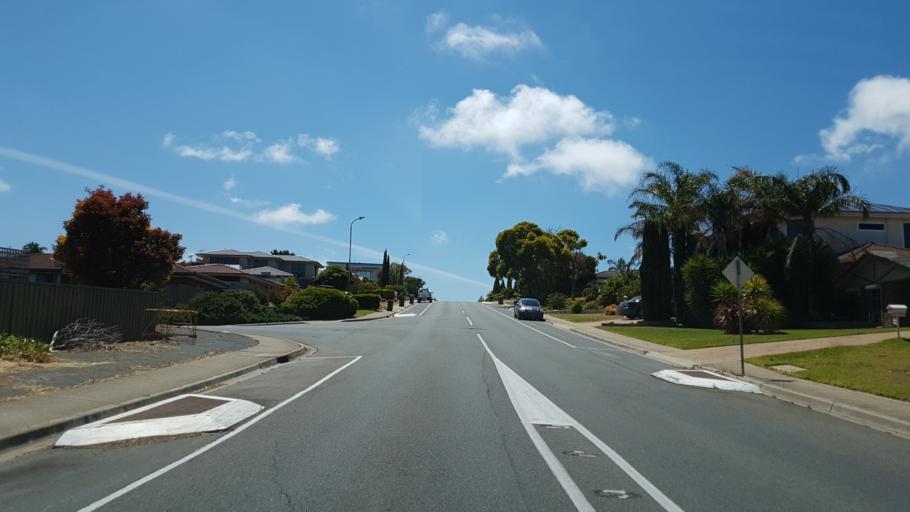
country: AU
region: South Australia
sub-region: Marion
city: Happy Valley
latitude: -35.0679
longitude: 138.5189
